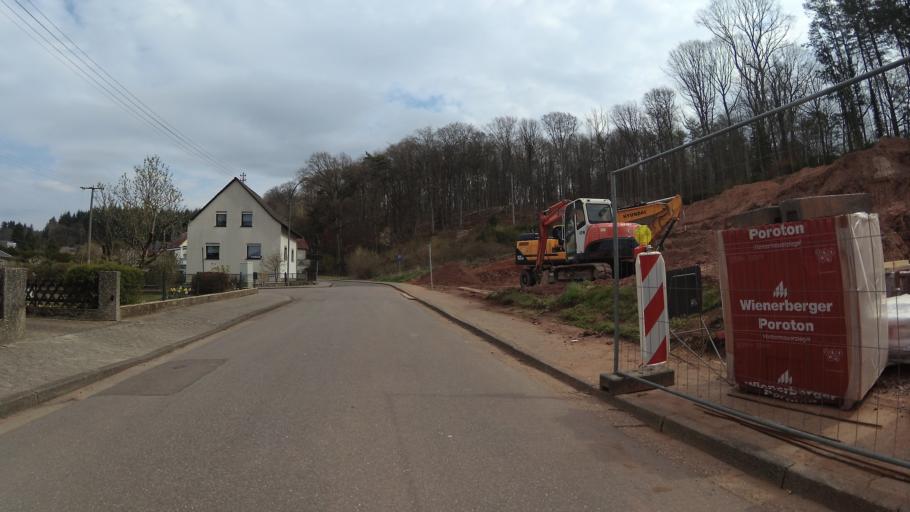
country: DE
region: Saarland
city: Mettlach
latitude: 49.4712
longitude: 6.6165
